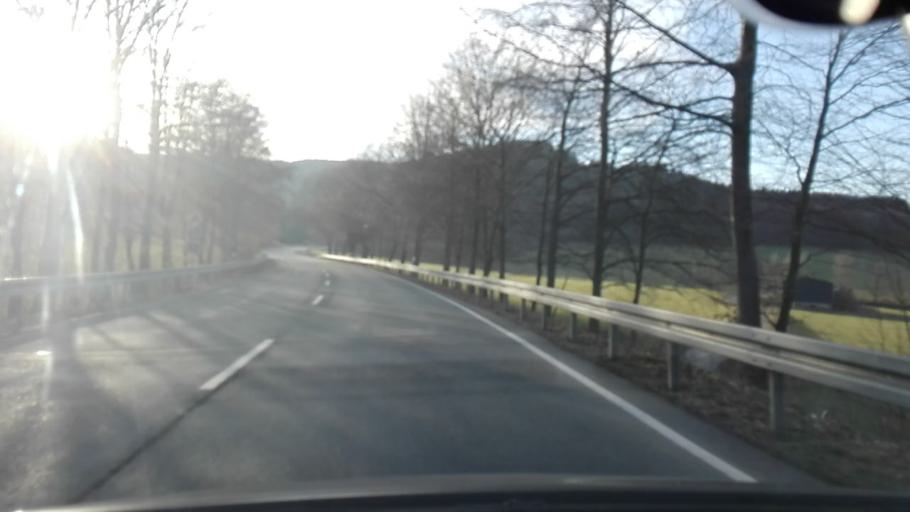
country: DE
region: North Rhine-Westphalia
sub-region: Regierungsbezirk Arnsberg
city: Schmallenberg
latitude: 51.1592
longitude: 8.1920
